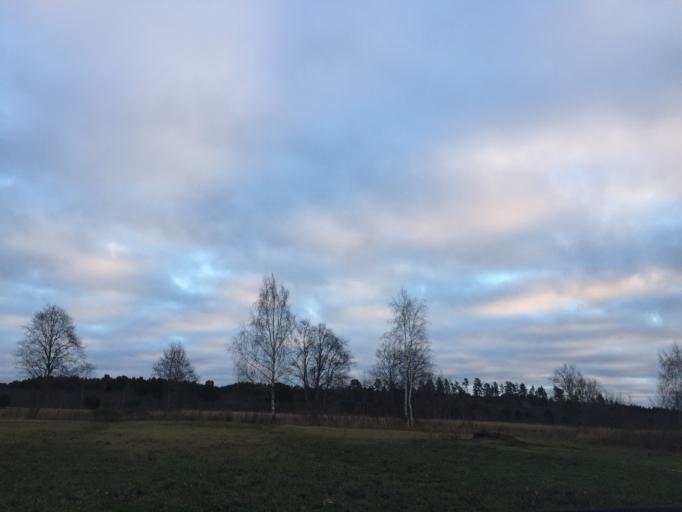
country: LV
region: Adazi
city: Adazi
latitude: 57.0660
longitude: 24.3453
